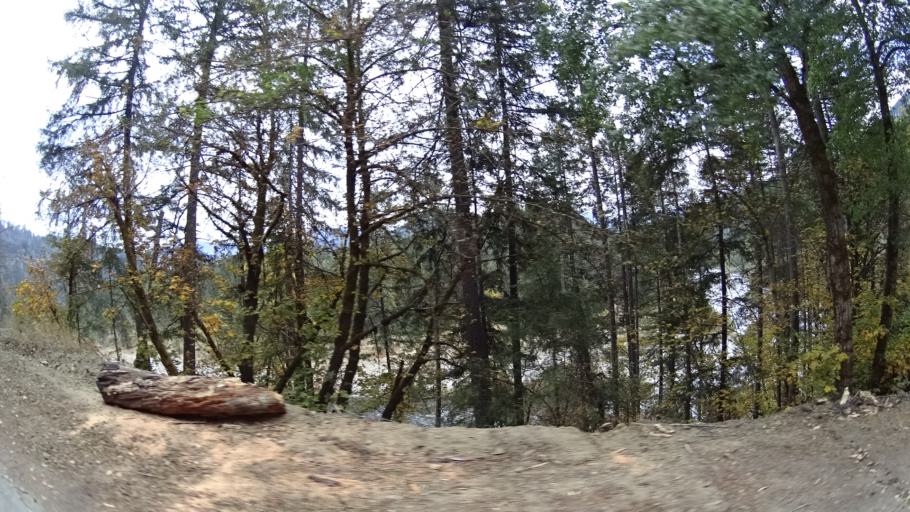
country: US
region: California
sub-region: Siskiyou County
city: Happy Camp
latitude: 41.7689
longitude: -123.3432
